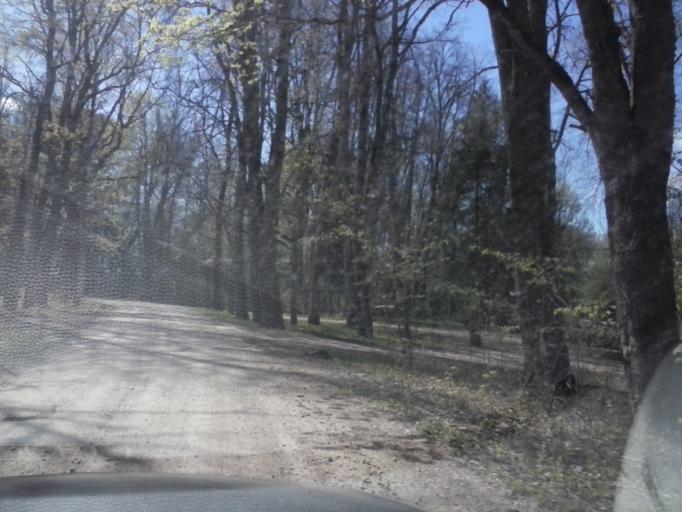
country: EE
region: Valgamaa
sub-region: Torva linn
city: Torva
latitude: 58.2340
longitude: 25.8922
